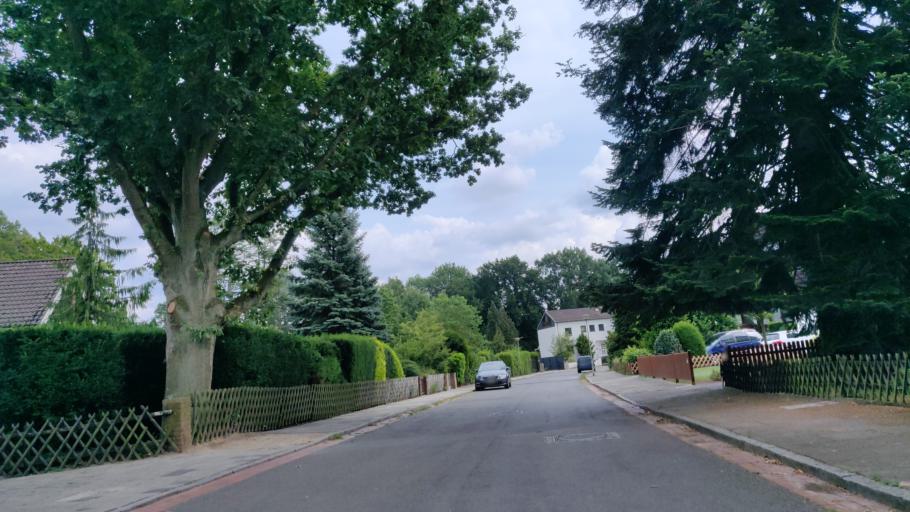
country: DE
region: Lower Saxony
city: Lilienthal
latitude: 53.1056
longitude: 8.8887
